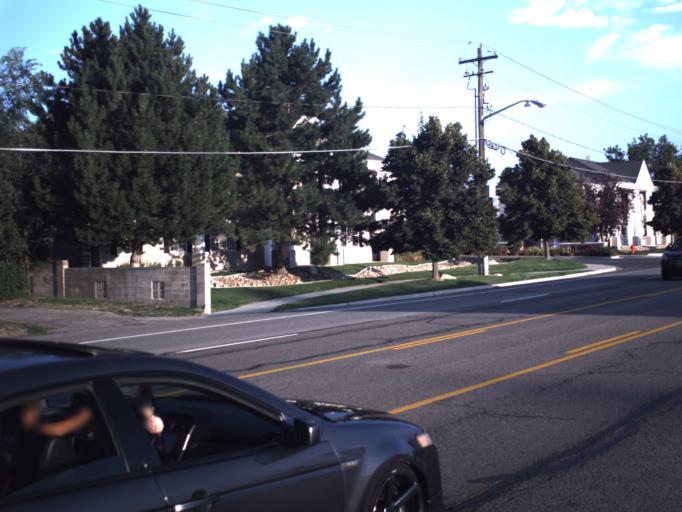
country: US
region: Utah
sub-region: Salt Lake County
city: White City
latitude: 40.5509
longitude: -111.8909
